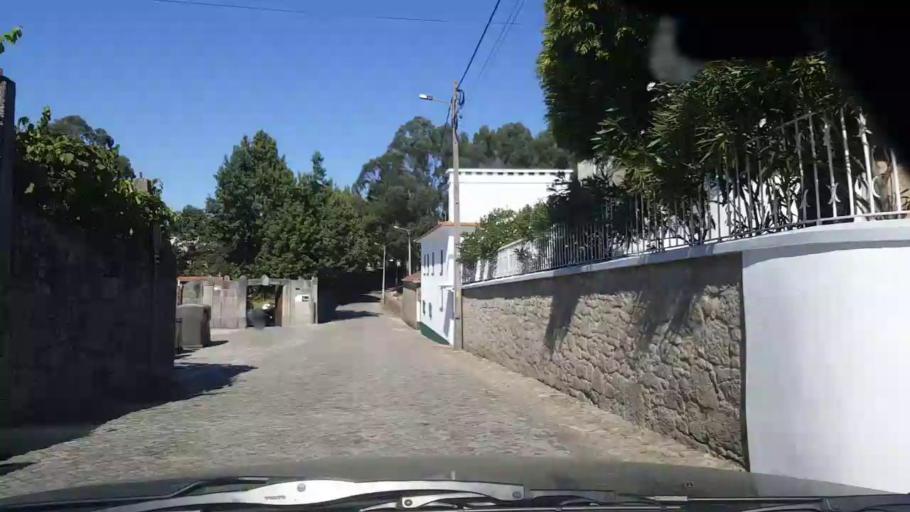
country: PT
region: Porto
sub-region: Vila do Conde
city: Arvore
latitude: 41.3269
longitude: -8.6733
